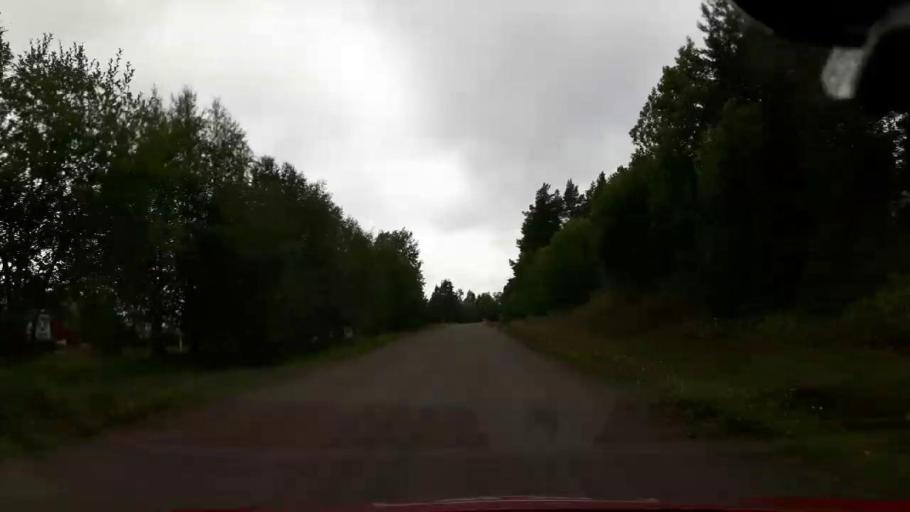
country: SE
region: Jaemtland
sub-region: Krokoms Kommun
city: Valla
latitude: 63.3573
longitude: 14.0962
